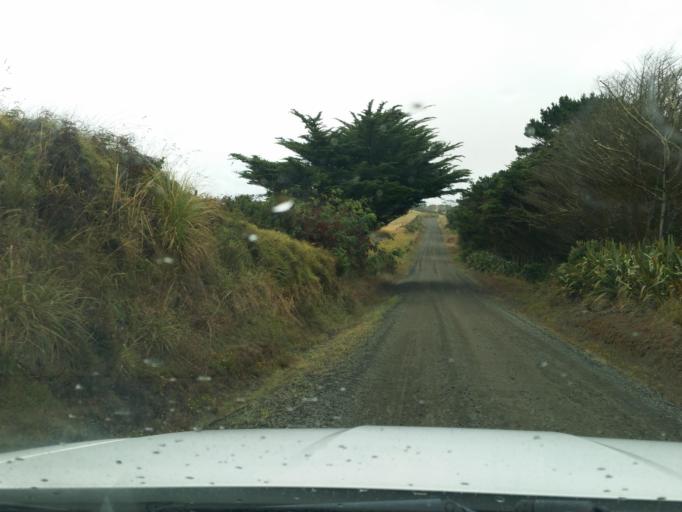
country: NZ
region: Northland
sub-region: Kaipara District
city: Dargaville
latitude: -36.0567
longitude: 173.8641
